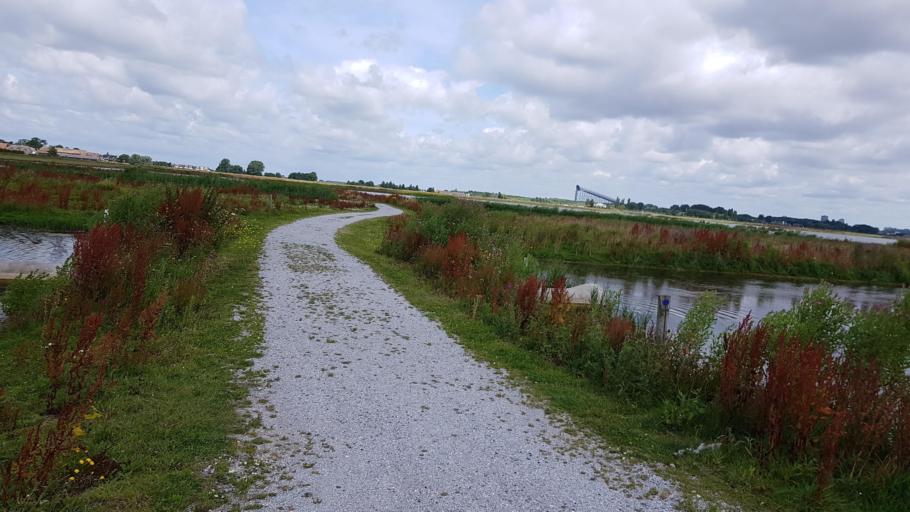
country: NL
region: South Holland
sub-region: Gemeente Pijnacker-Nootdorp
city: Pijnacker
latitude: 52.0711
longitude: 4.4239
